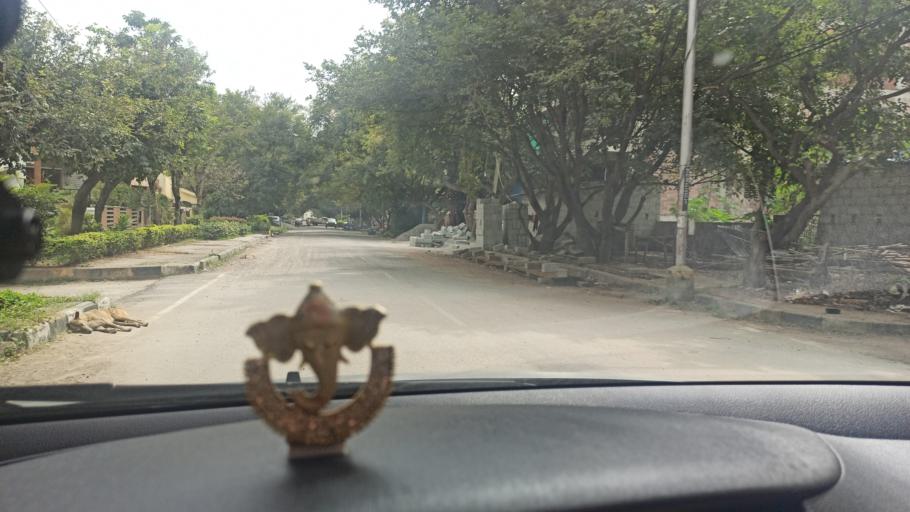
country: IN
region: Karnataka
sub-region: Bangalore Urban
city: Bangalore
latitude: 12.9166
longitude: 77.6256
